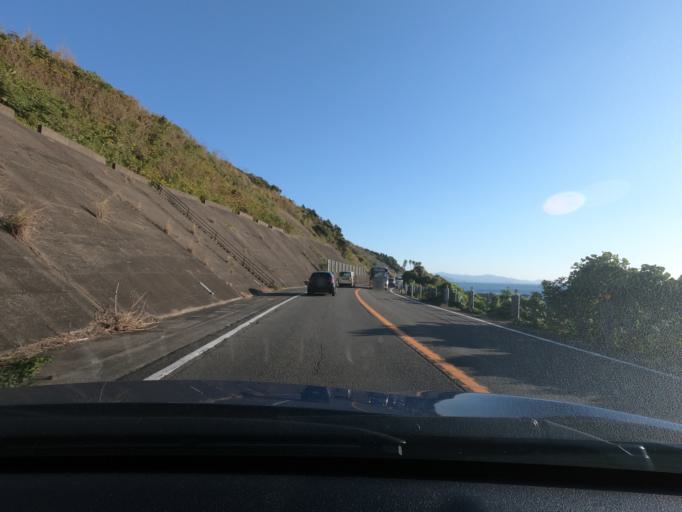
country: JP
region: Kagoshima
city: Akune
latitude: 31.9649
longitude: 130.2125
